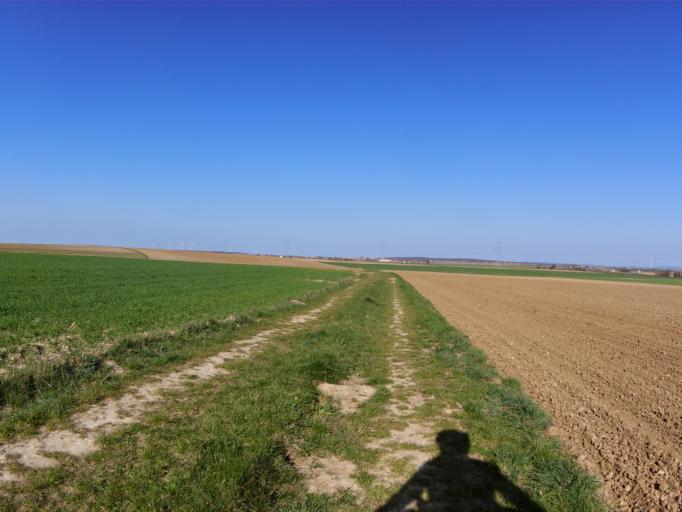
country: DE
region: Bavaria
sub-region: Regierungsbezirk Unterfranken
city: Oberpleichfeld
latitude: 49.8326
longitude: 10.0758
